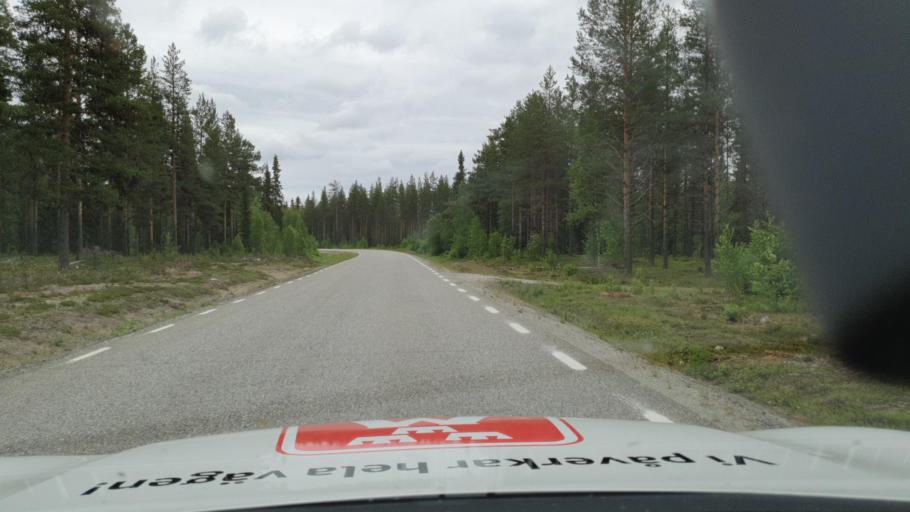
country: SE
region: Vaesterbotten
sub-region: Lycksele Kommun
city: Lycksele
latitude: 64.1958
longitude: 18.3015
